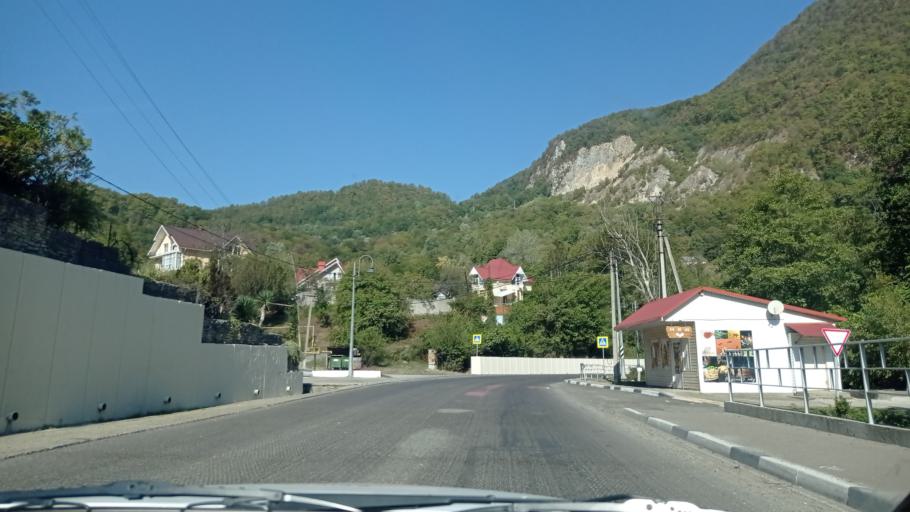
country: RU
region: Krasnodarskiy
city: Vysokoye
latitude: 43.5900
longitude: 40.0072
